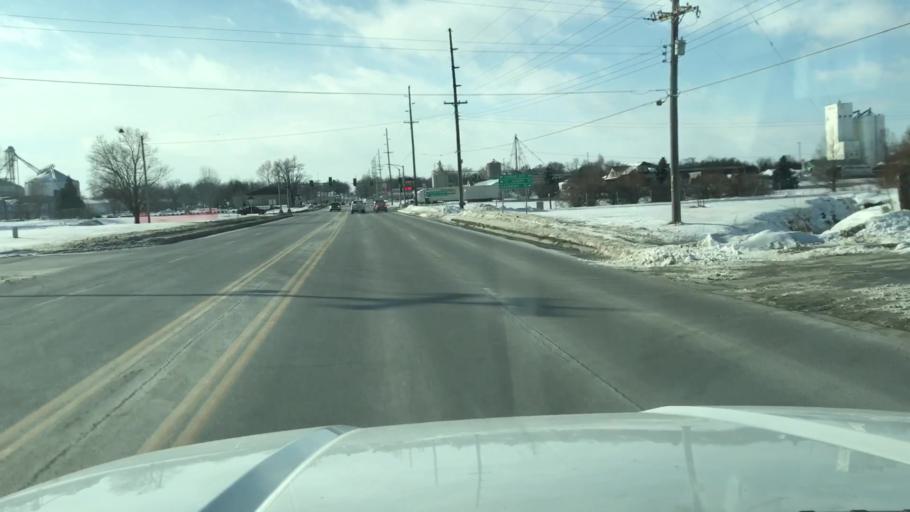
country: US
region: Missouri
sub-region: Nodaway County
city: Maryville
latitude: 40.3453
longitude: -94.8500
